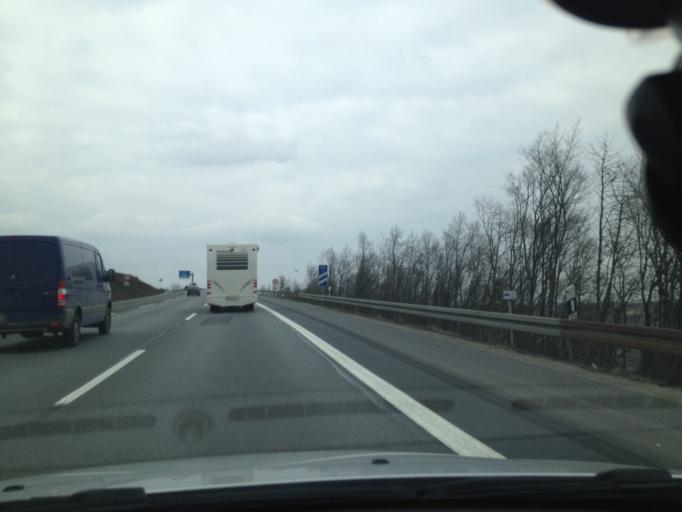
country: DE
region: Bavaria
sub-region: Regierungsbezirk Unterfranken
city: Randersacker
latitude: 49.7502
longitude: 9.9651
